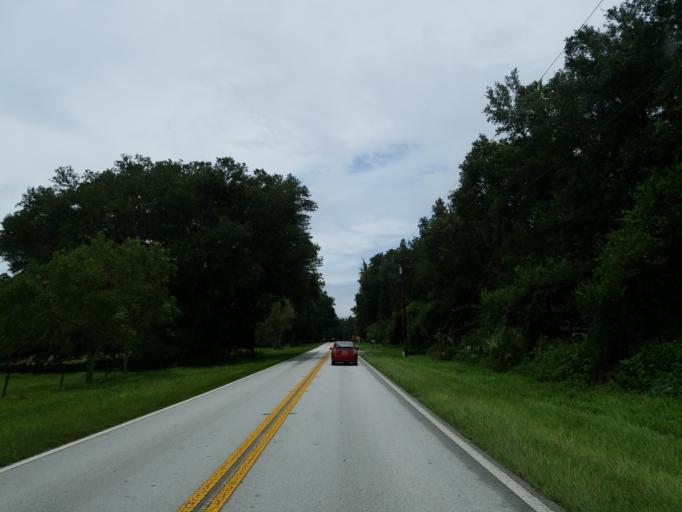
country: US
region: Florida
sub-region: Sumter County
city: Bushnell
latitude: 28.6862
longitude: -82.1953
